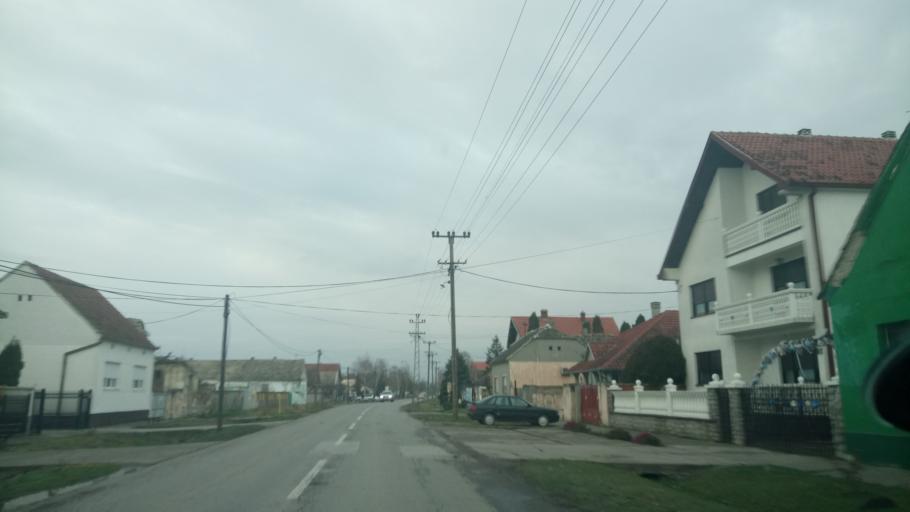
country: RS
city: Vojka
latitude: 44.9437
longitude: 20.1535
